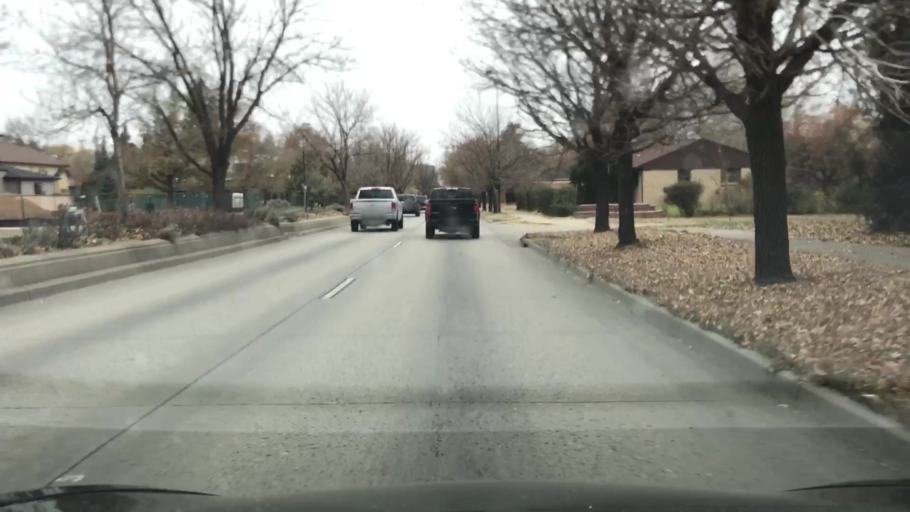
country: US
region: Colorado
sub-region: Arapahoe County
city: Glendale
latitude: 39.6785
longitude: -104.9462
